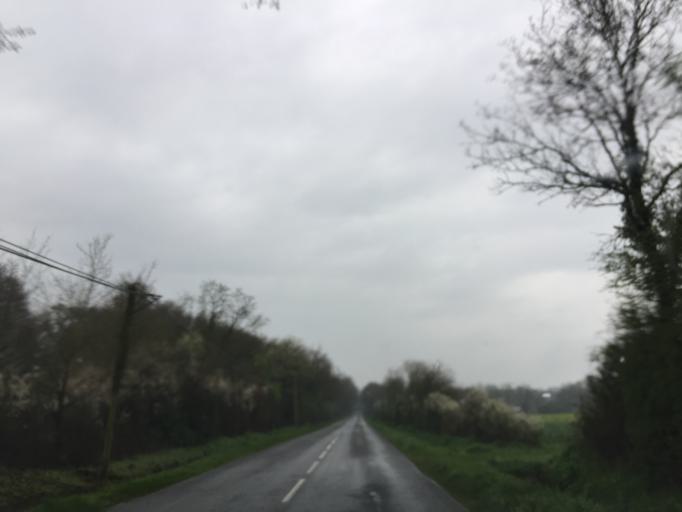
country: FR
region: Pays de la Loire
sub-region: Departement de la Loire-Atlantique
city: Casson
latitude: 47.3763
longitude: -1.5209
